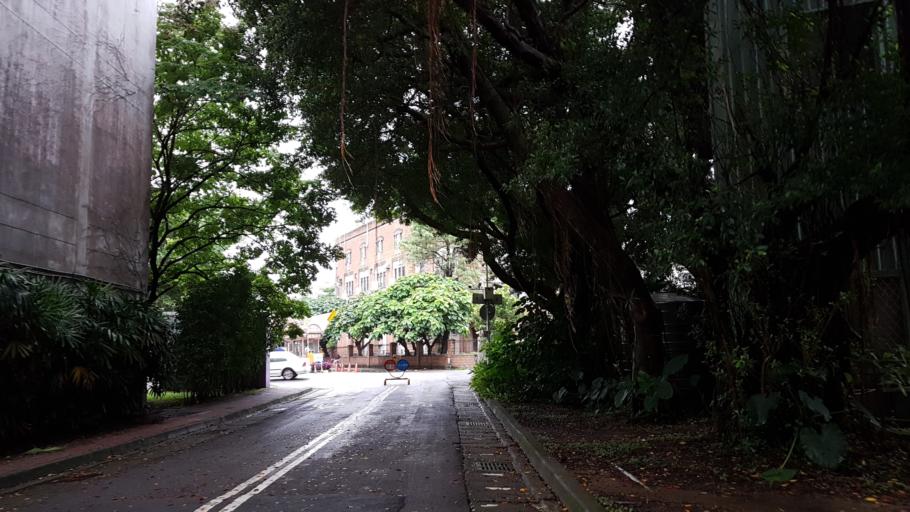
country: TW
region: Taipei
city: Taipei
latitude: 25.0181
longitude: 121.5433
